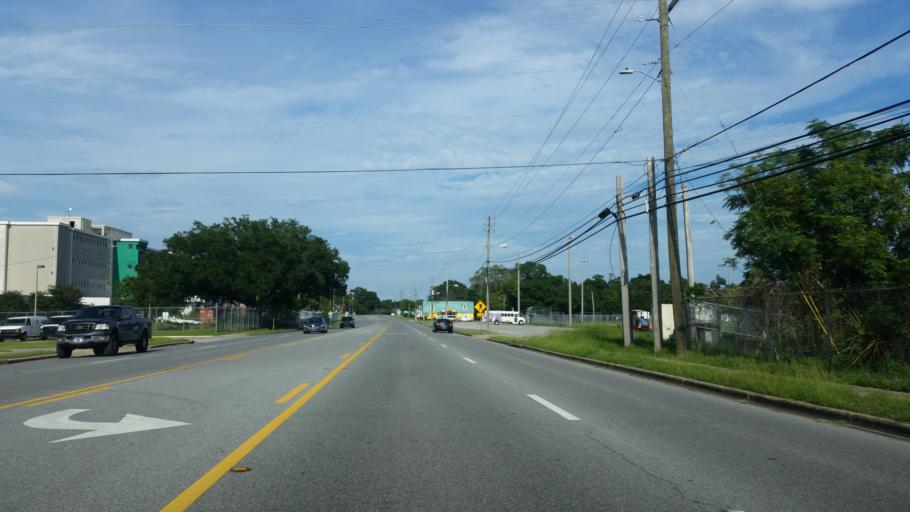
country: US
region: Florida
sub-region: Escambia County
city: Goulding
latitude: 30.4415
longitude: -87.2344
